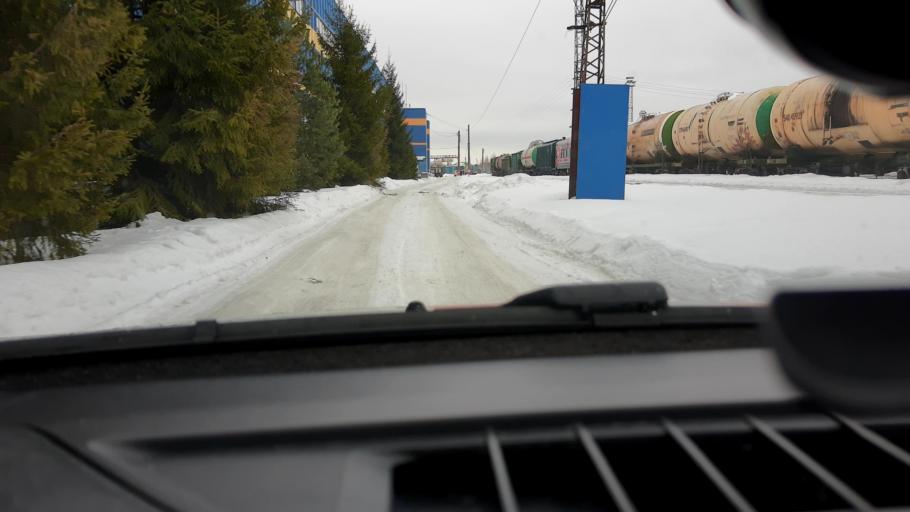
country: RU
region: Nizjnij Novgorod
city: Gorbatovka
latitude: 56.2834
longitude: 43.8536
